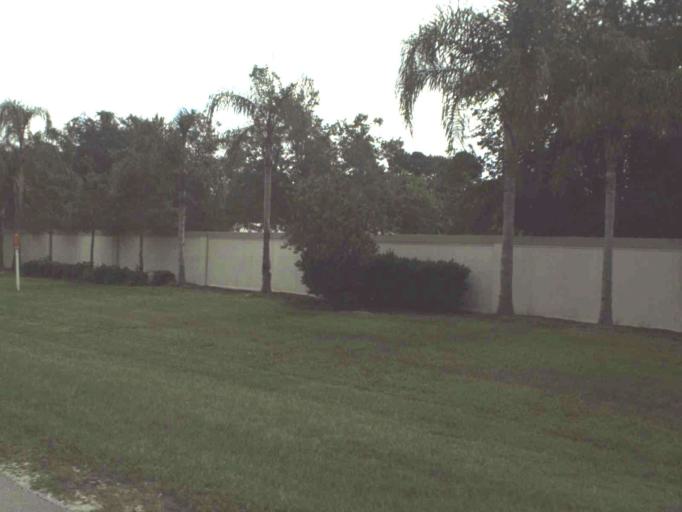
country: US
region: Florida
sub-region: Volusia County
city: Samsula-Spruce Creek
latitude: 28.9988
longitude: -81.0708
